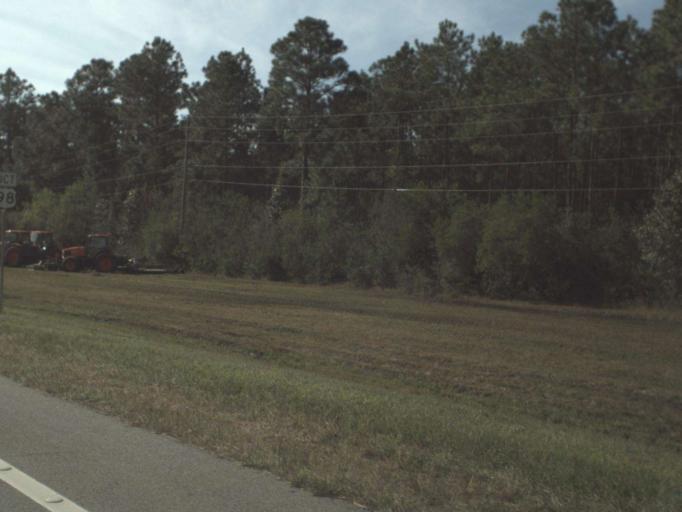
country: US
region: Florida
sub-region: Escambia County
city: Myrtle Grove
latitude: 30.4058
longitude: -87.3424
